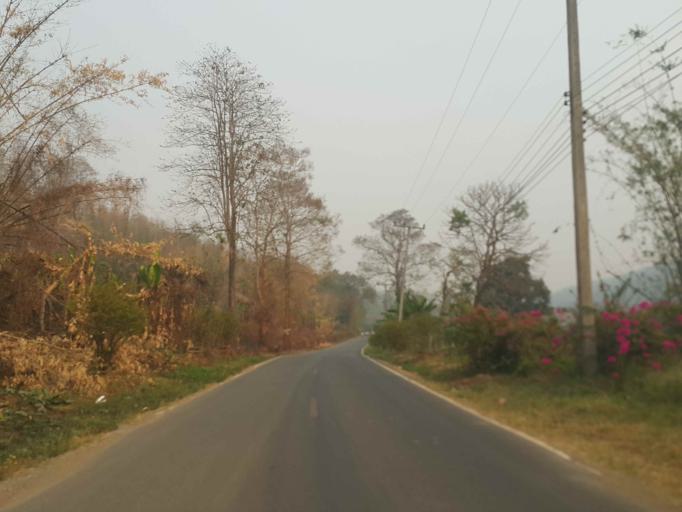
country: TH
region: Chiang Mai
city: Mae Taeng
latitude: 19.1341
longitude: 98.8796
